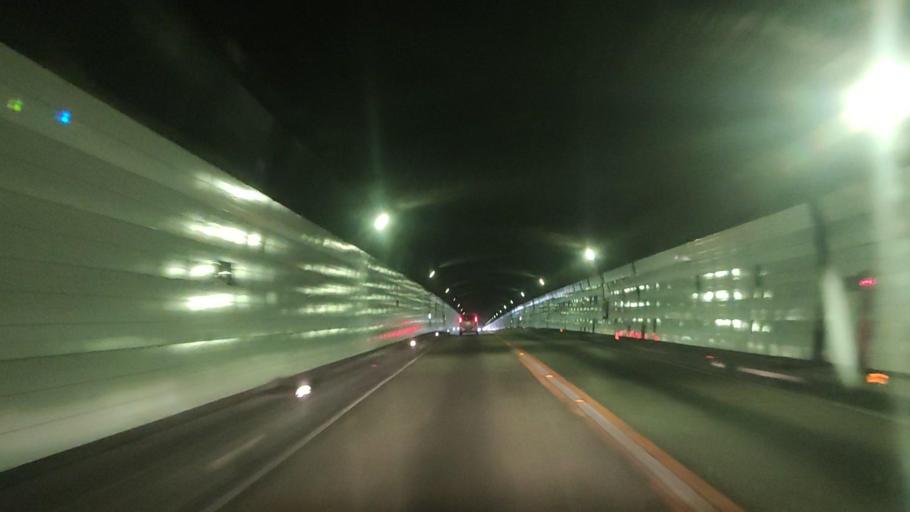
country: JP
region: Kumamoto
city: Hitoyoshi
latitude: 32.0973
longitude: 130.8034
